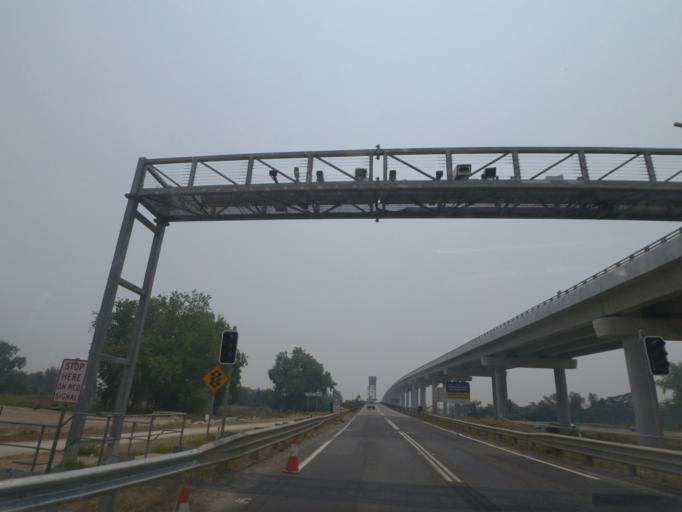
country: AU
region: New South Wales
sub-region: Clarence Valley
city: Maclean
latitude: -29.4350
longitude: 153.2407
